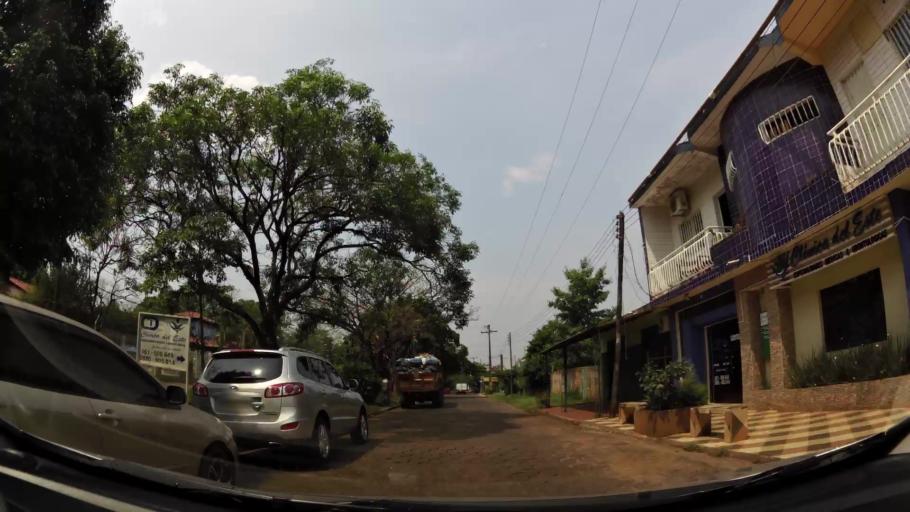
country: PY
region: Alto Parana
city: Presidente Franco
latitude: -25.5424
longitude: -54.6298
